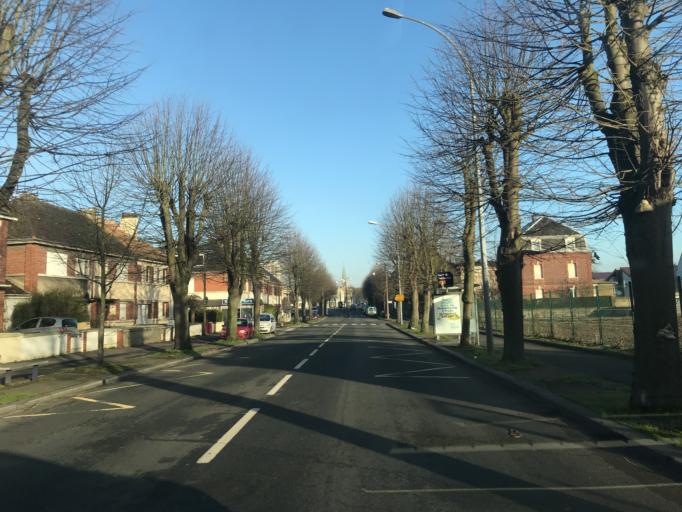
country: FR
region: Haute-Normandie
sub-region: Departement de la Seine-Maritime
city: Sotteville-les-Rouen
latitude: 49.4114
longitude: 1.0995
